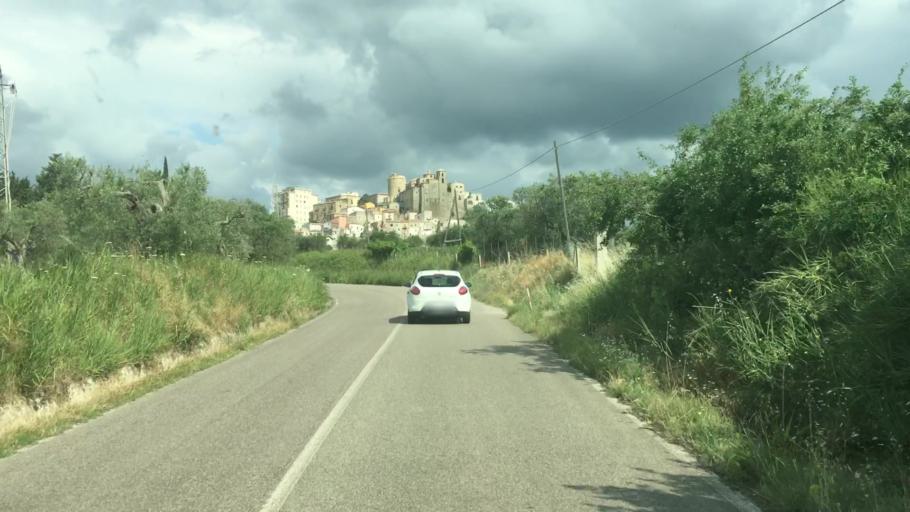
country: IT
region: Basilicate
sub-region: Provincia di Matera
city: San Mauro Forte
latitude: 40.4826
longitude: 16.2576
